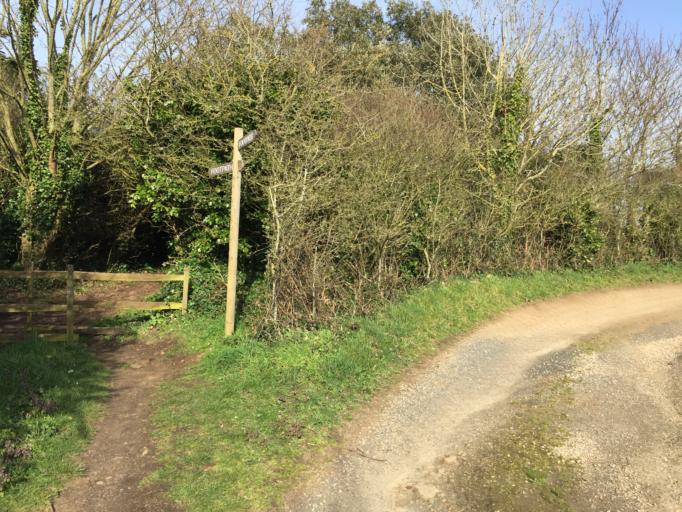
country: JE
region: St Helier
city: Saint Helier
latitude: 49.2502
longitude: -2.1704
